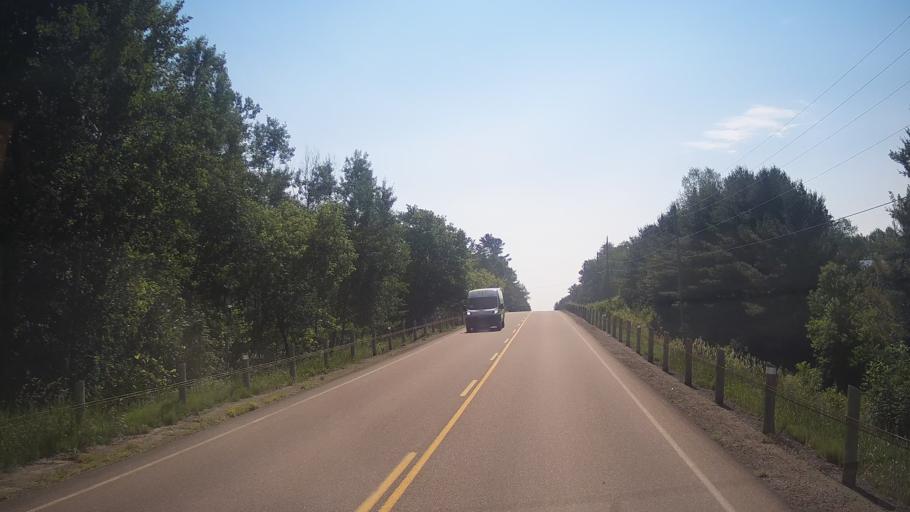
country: CA
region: Ontario
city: Pembroke
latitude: 45.6172
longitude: -77.1772
